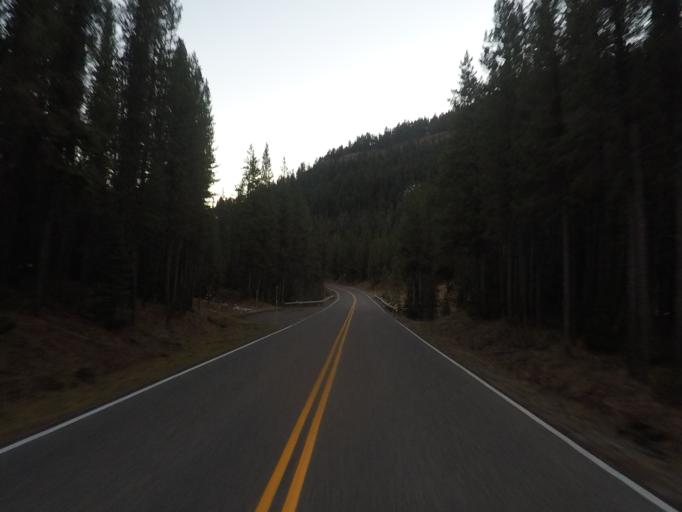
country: US
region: Montana
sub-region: Stillwater County
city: Absarokee
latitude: 44.9457
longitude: -110.0817
